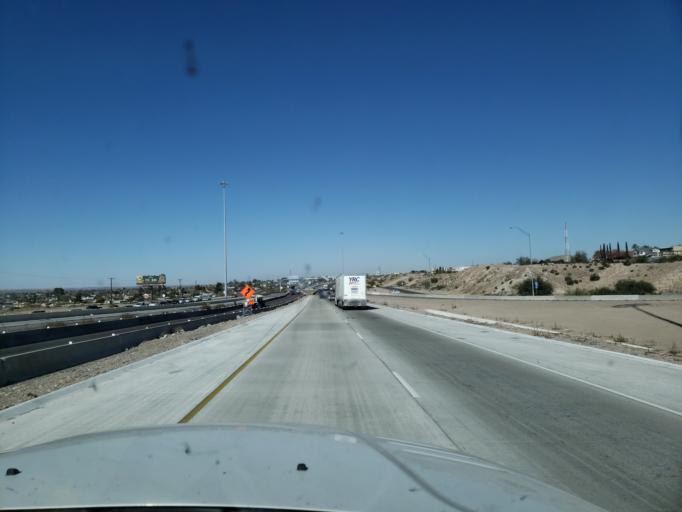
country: US
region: New Mexico
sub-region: Dona Ana County
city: Sunland Park
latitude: 31.8417
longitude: -106.5710
